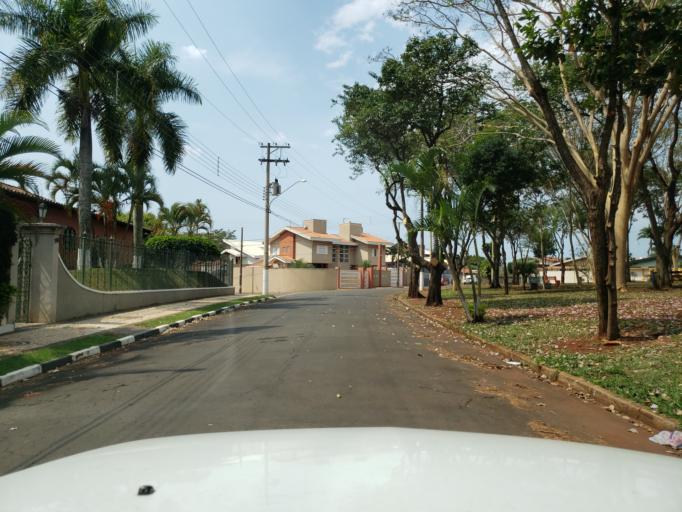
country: BR
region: Sao Paulo
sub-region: Moji-Guacu
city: Mogi-Gaucu
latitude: -22.3665
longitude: -46.9388
